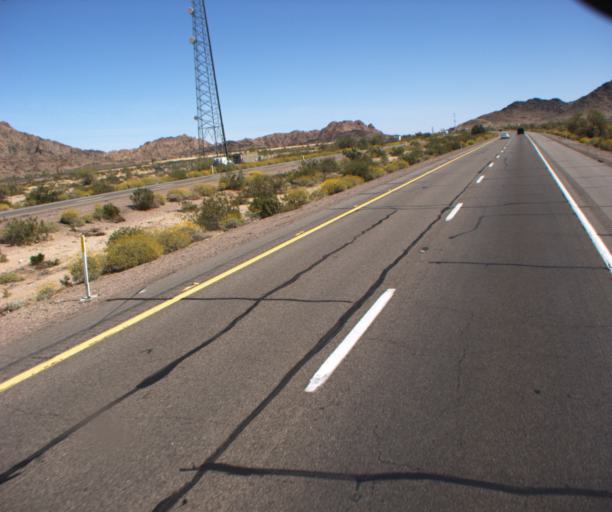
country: US
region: Arizona
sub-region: Yuma County
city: Wellton
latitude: 32.7217
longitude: -113.7664
